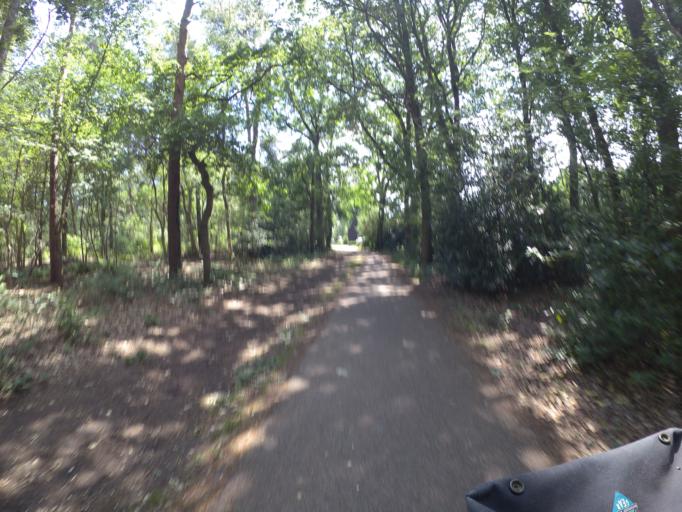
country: NL
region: North Brabant
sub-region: Gemeente Oisterwijk
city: Oisterwijk
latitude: 51.5538
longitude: 5.2119
